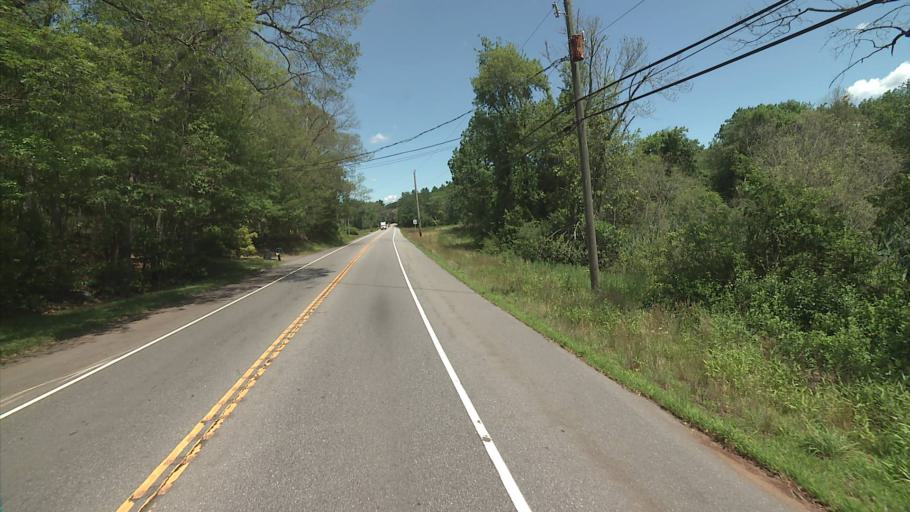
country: US
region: Connecticut
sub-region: New London County
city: Old Mystic
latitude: 41.4587
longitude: -71.9083
